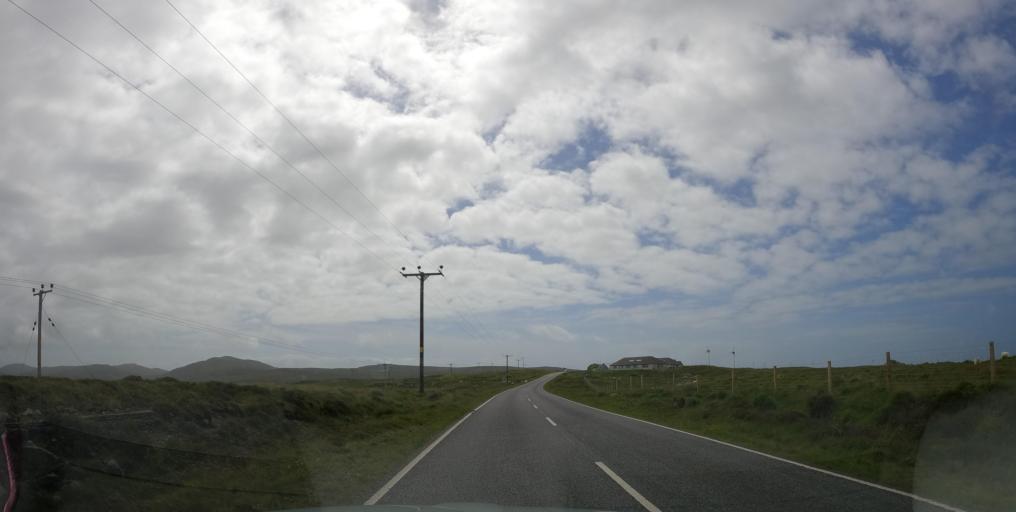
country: GB
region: Scotland
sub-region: Eilean Siar
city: Isle of South Uist
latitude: 57.2523
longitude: -7.3765
